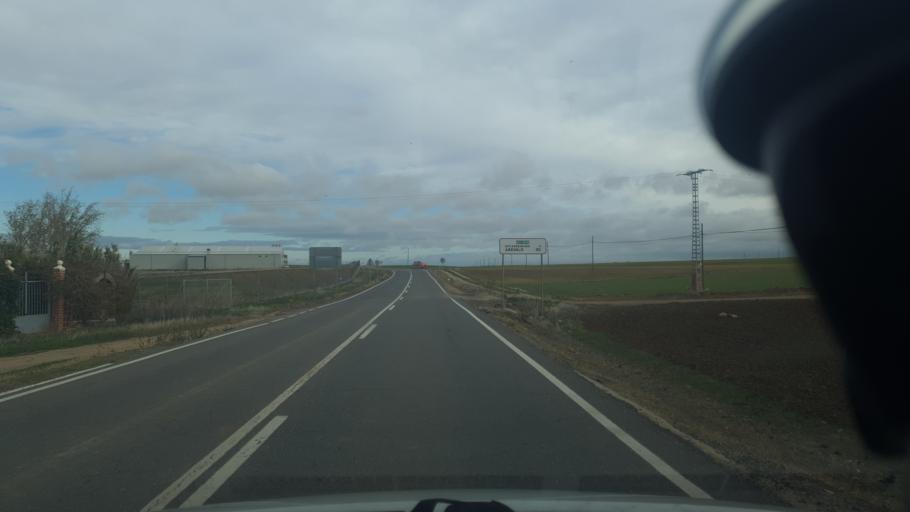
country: ES
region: Castille and Leon
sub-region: Provincia de Avila
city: Gotarrendura
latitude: 40.8056
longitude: -4.7581
